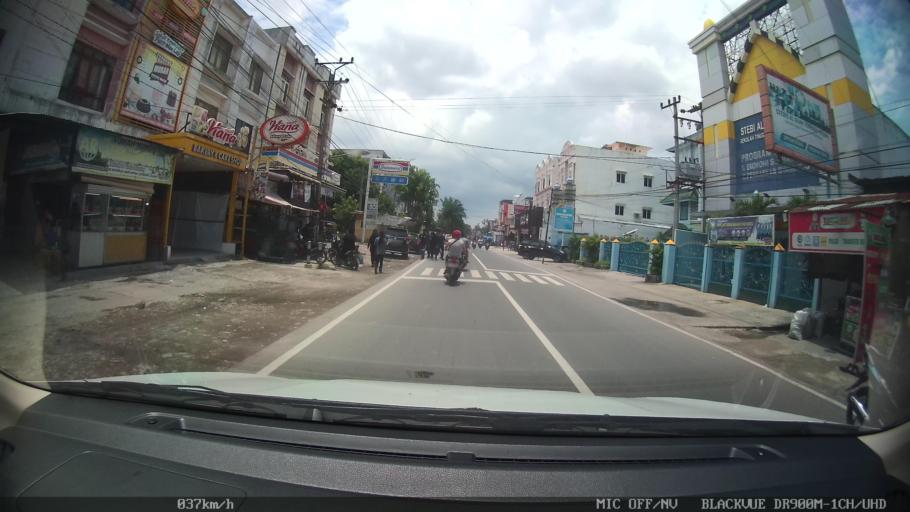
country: ID
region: North Sumatra
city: Medan
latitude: 3.6159
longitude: 98.6989
